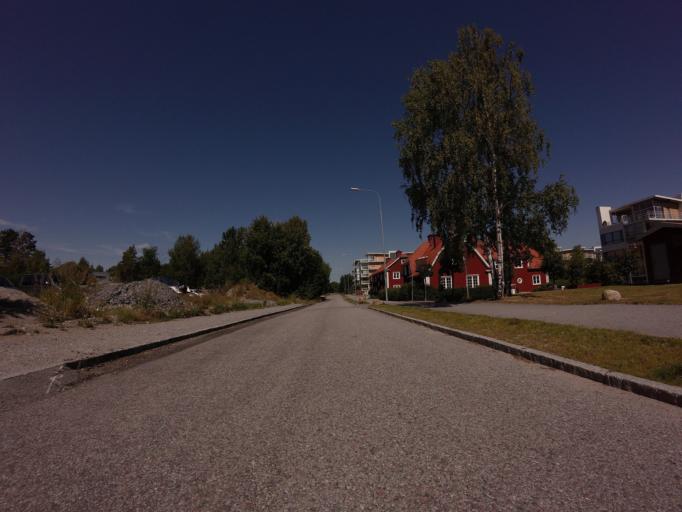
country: SE
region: Stockholm
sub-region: Lidingo
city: Brevik
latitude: 59.3575
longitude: 18.2292
